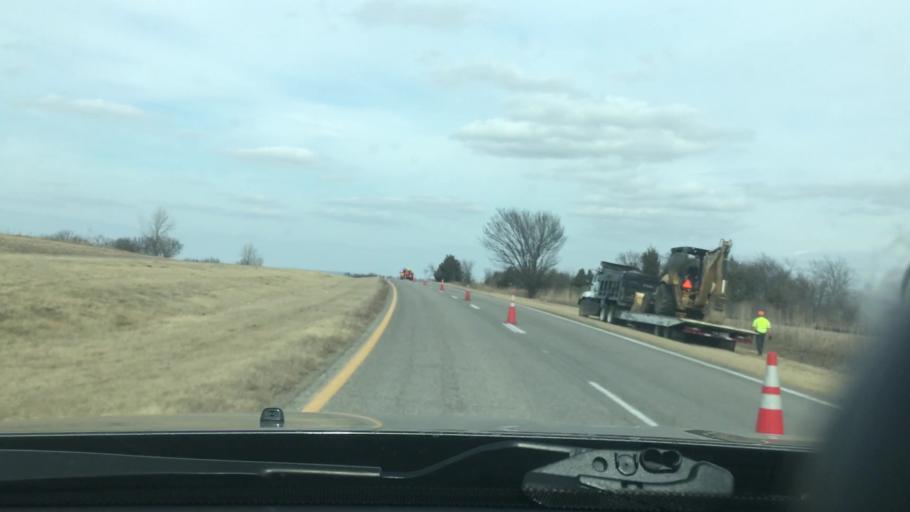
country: US
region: Oklahoma
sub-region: Pontotoc County
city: Ada
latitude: 34.7047
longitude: -96.7315
